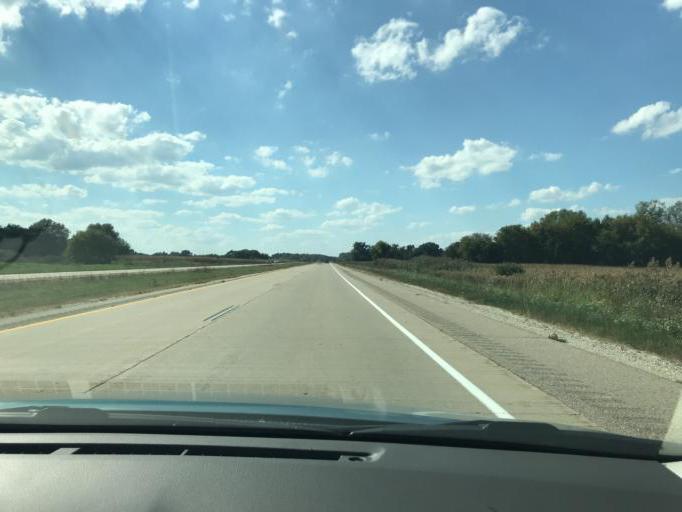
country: US
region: Wisconsin
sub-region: Kenosha County
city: Twin Lakes
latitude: 42.5813
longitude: -88.2398
